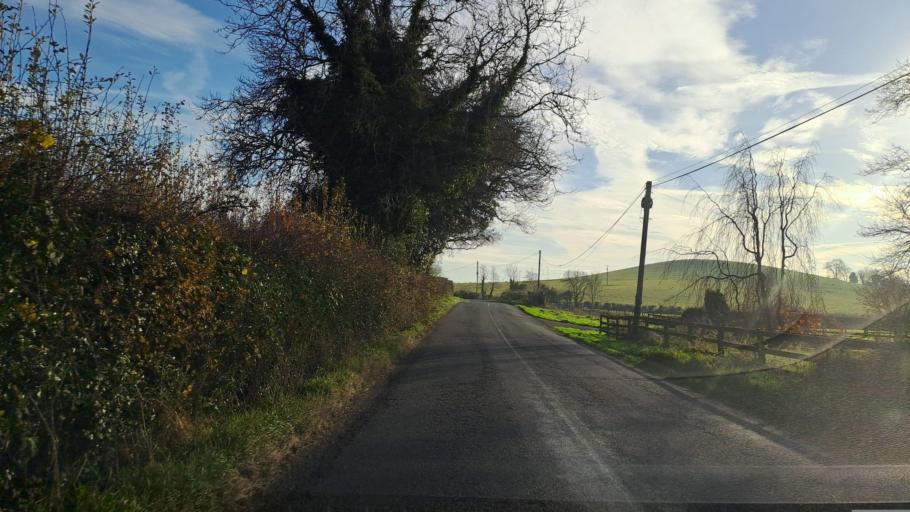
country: IE
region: Ulster
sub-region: County Monaghan
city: Carrickmacross
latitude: 53.8604
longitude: -6.6767
